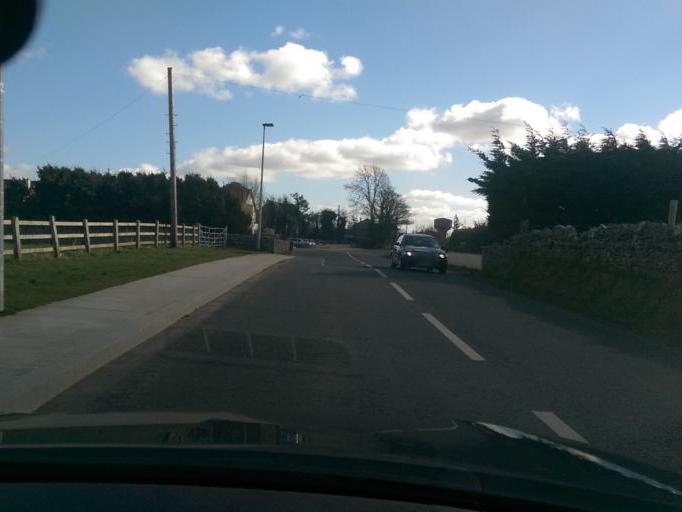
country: IE
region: Connaught
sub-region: County Galway
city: Athenry
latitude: 53.3087
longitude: -8.7538
